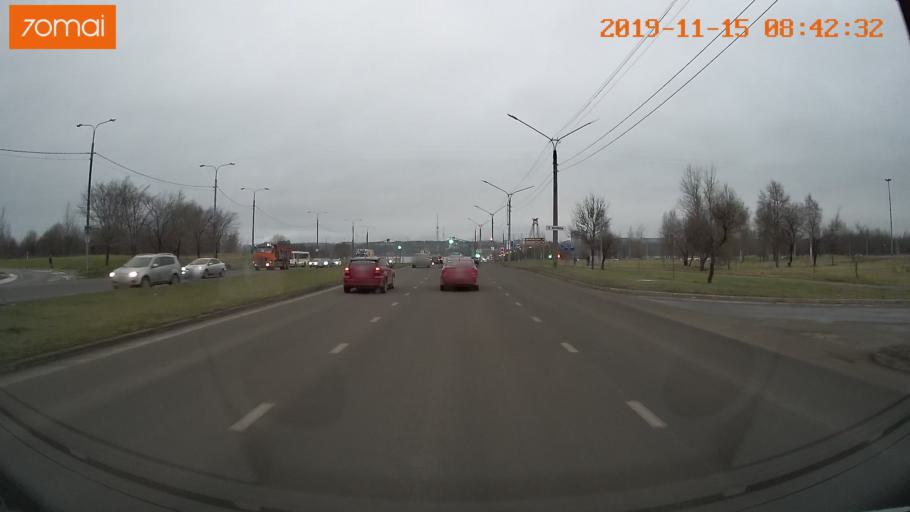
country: RU
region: Vologda
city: Cherepovets
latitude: 59.1035
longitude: 37.9074
